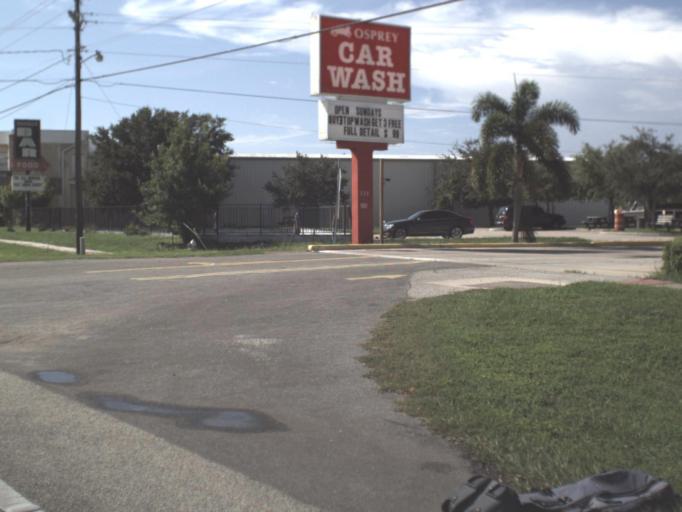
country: US
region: Florida
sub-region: Sarasota County
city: Osprey
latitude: 27.1855
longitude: -82.4853
